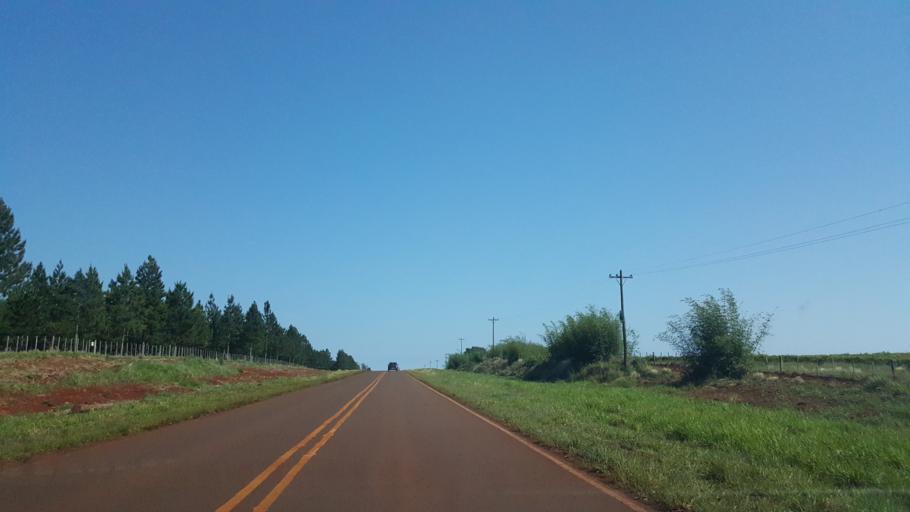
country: AR
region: Misiones
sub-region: Departamento de Apostoles
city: San Jose
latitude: -27.7854
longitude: -55.8340
